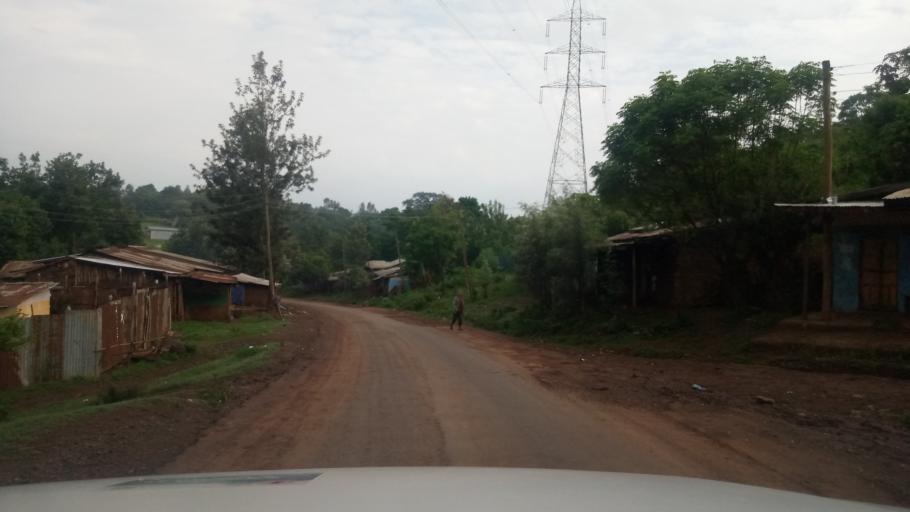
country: ET
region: Oromiya
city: Agaro
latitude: 7.8360
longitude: 36.6778
